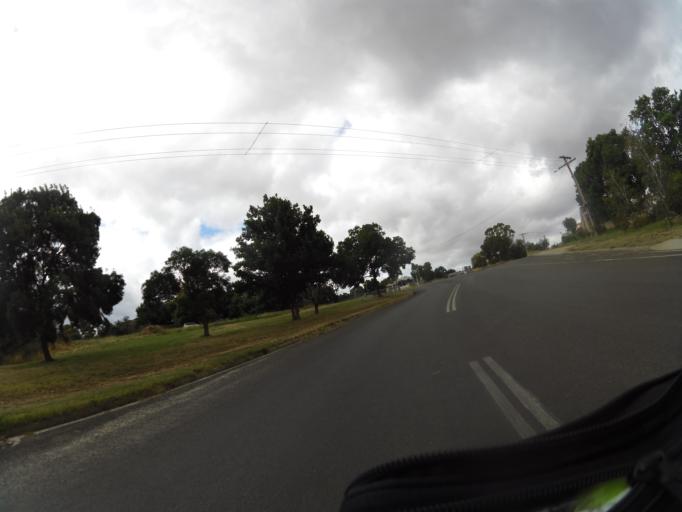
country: AU
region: Victoria
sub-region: Mount Alexander
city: Castlemaine
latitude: -37.0722
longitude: 144.2106
